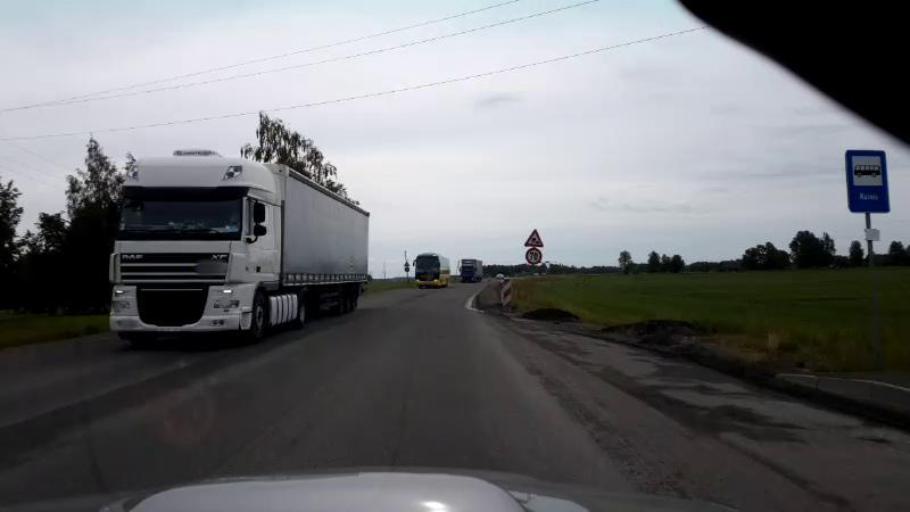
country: LV
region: Bauskas Rajons
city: Bauska
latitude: 56.3076
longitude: 24.3393
